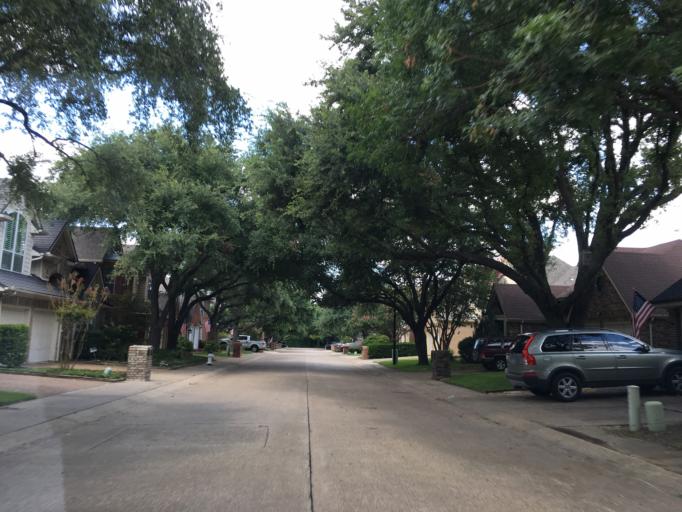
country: US
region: Texas
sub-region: Dallas County
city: Addison
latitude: 32.9475
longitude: -96.8482
